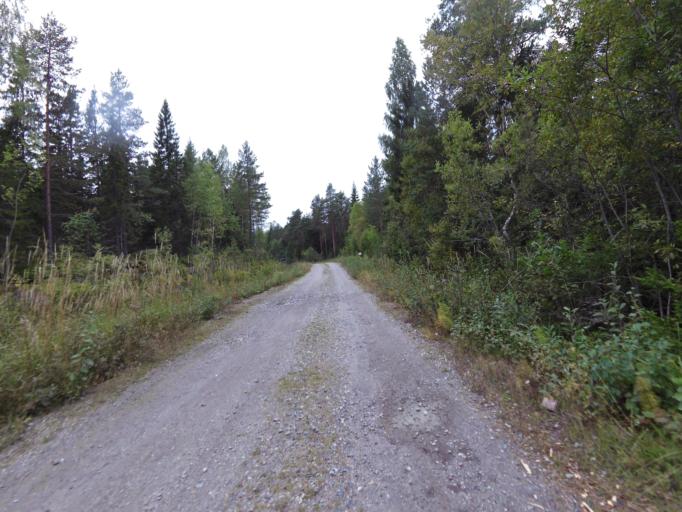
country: SE
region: Gaevleborg
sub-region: Gavle Kommun
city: Valbo
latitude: 60.7448
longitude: 17.0040
